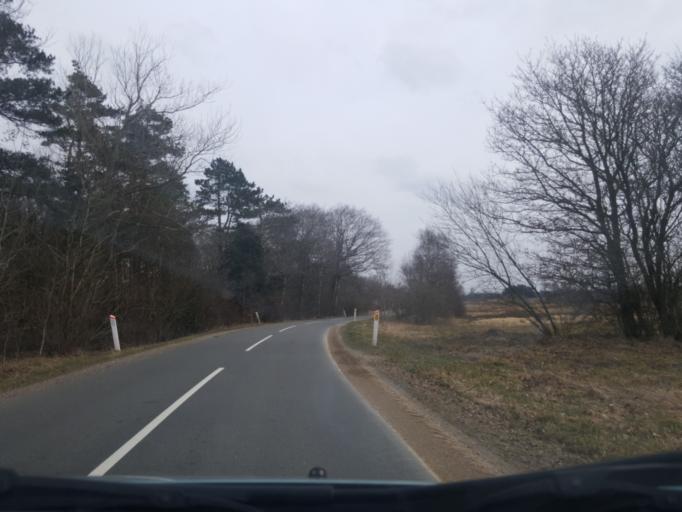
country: DK
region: Central Jutland
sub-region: Holstebro Kommune
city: Ulfborg
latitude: 56.2019
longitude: 8.2523
